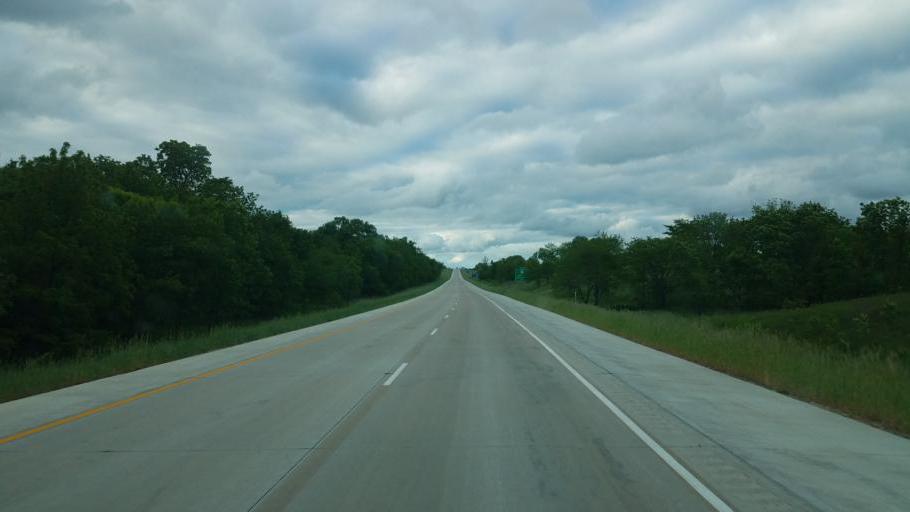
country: US
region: Iowa
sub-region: Decatur County
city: Lamoni
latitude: 40.6042
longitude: -93.9044
